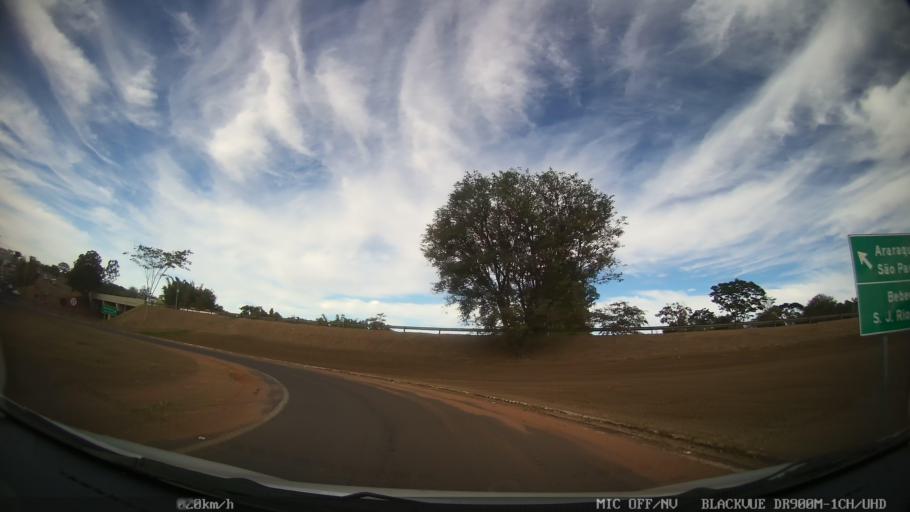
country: BR
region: Sao Paulo
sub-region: Catanduva
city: Catanduva
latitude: -21.1431
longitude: -49.0078
